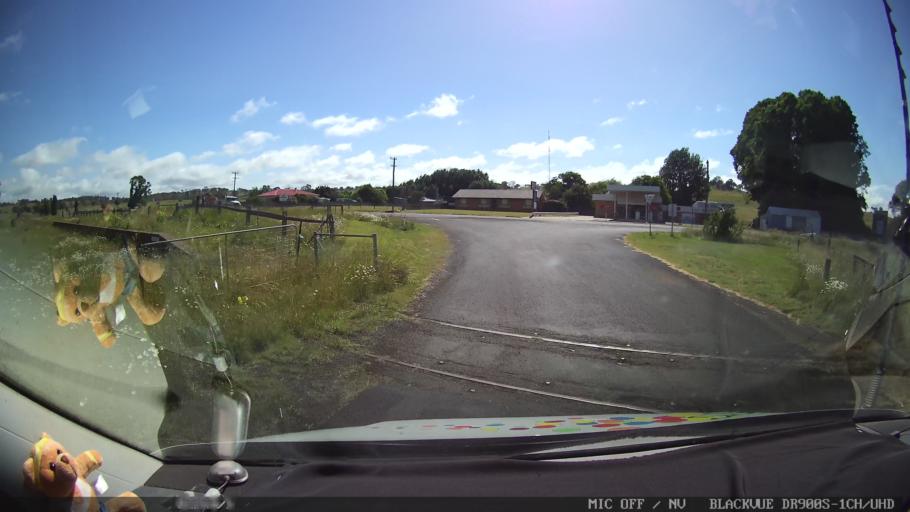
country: AU
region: New South Wales
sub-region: Guyra
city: Guyra
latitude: -30.1288
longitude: 151.6836
